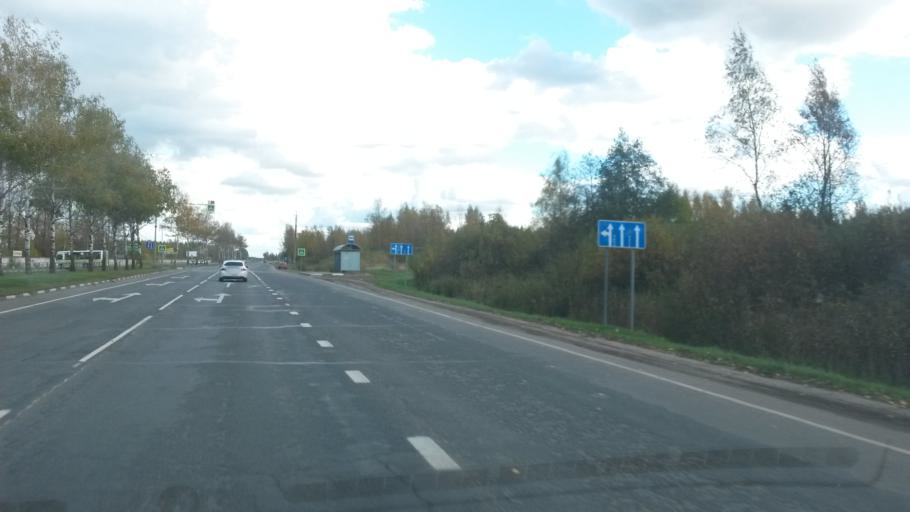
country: RU
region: Jaroslavl
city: Yaroslavl
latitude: 57.5408
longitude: 39.9771
